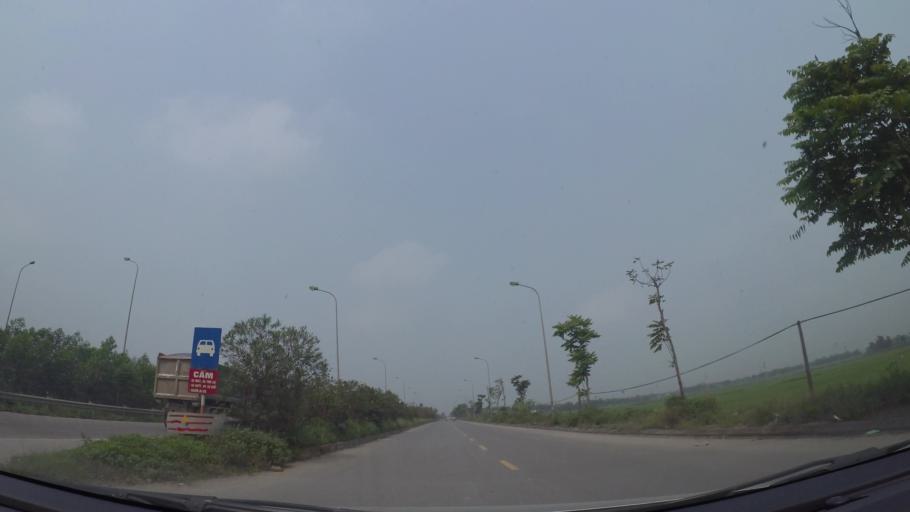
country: VN
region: Ha Noi
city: Quoc Oai
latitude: 21.0020
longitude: 105.6190
